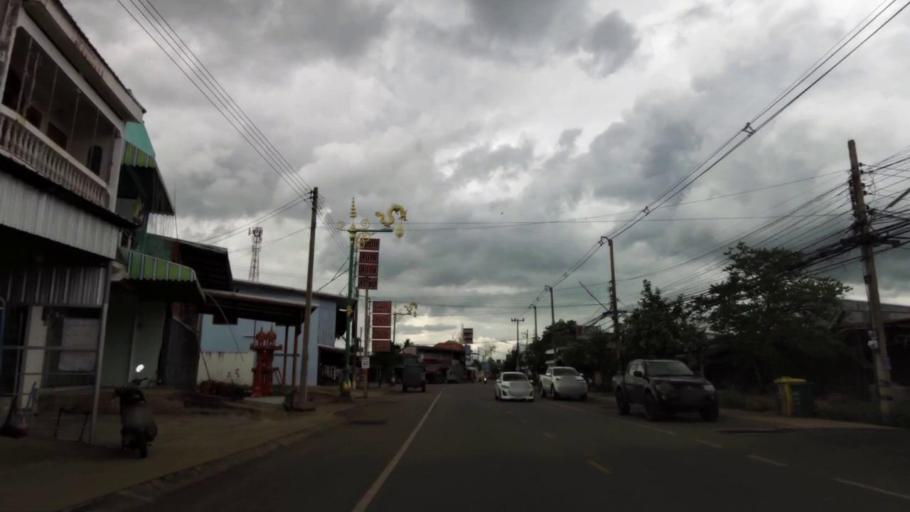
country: TH
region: Nakhon Sawan
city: Phai Sali
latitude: 15.5989
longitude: 100.6478
